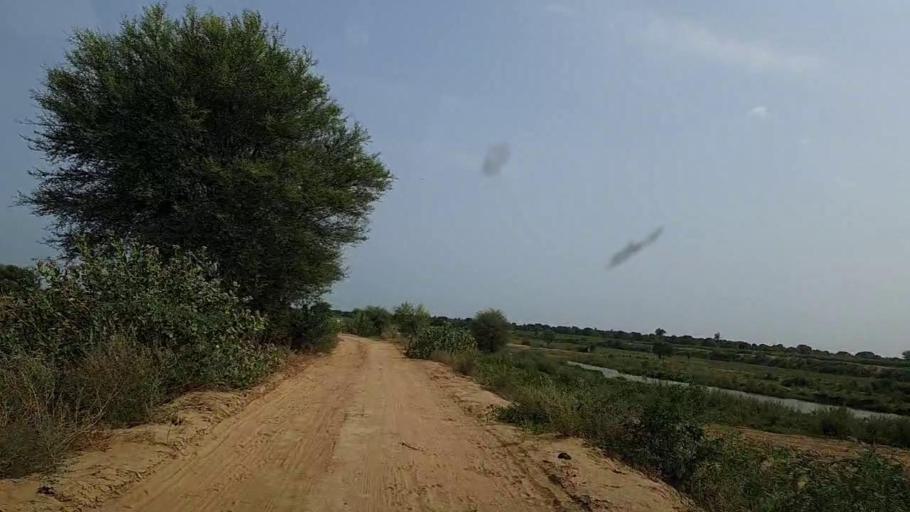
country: PK
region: Sindh
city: Kotri
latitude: 25.2586
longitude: 68.2619
